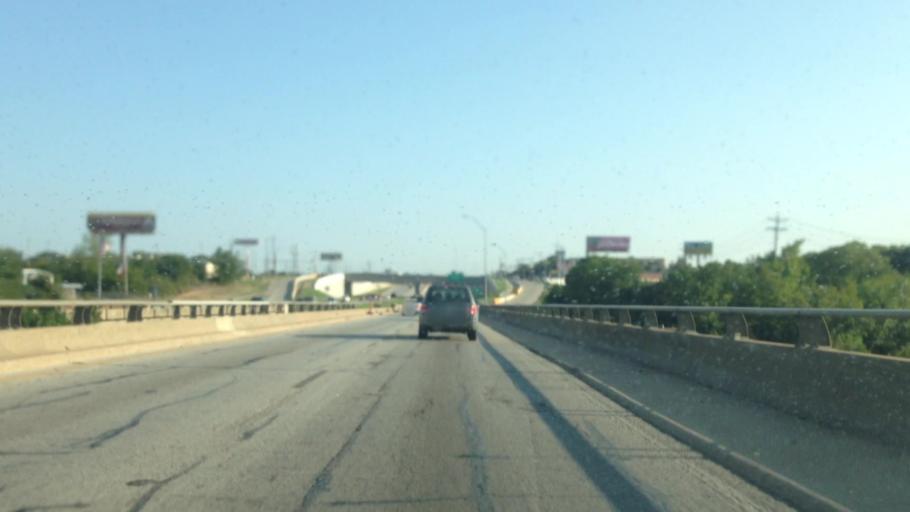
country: US
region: Texas
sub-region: Tarrant County
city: Richland Hills
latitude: 32.7817
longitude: -97.2128
